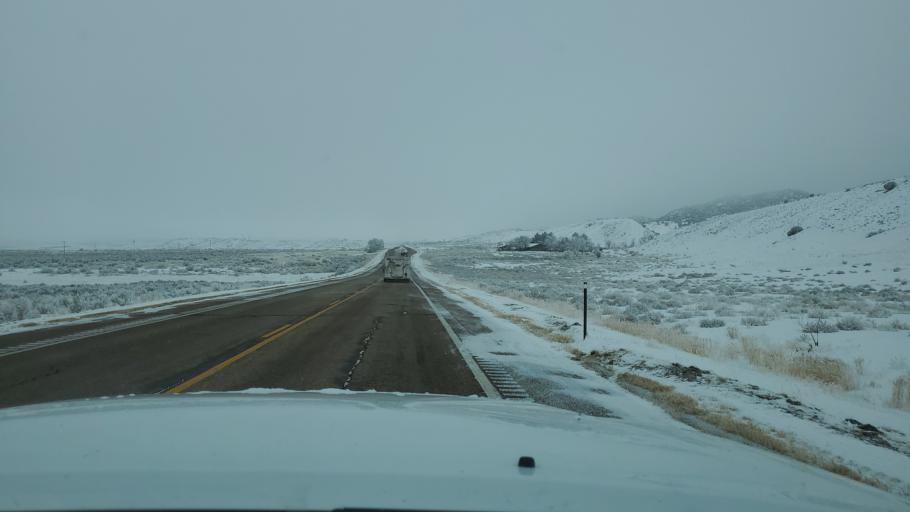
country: US
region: Colorado
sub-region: Rio Blanco County
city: Rangely
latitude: 40.2428
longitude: -108.9673
